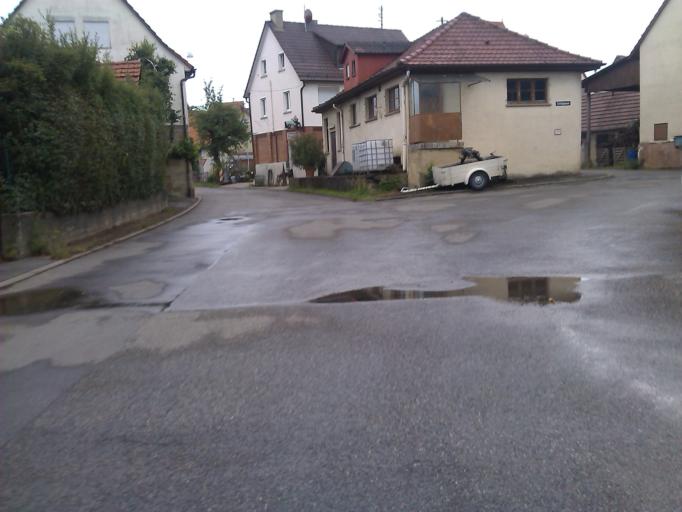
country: DE
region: Baden-Wuerttemberg
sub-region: Regierungsbezirk Stuttgart
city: Nordheim
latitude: 49.0787
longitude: 9.1049
